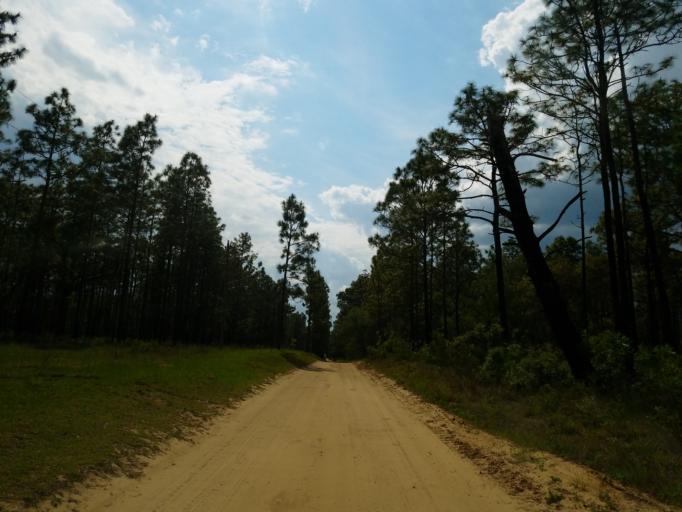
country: US
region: Florida
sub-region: Hernando County
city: Hill 'n Dale
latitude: 28.5575
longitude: -82.2735
